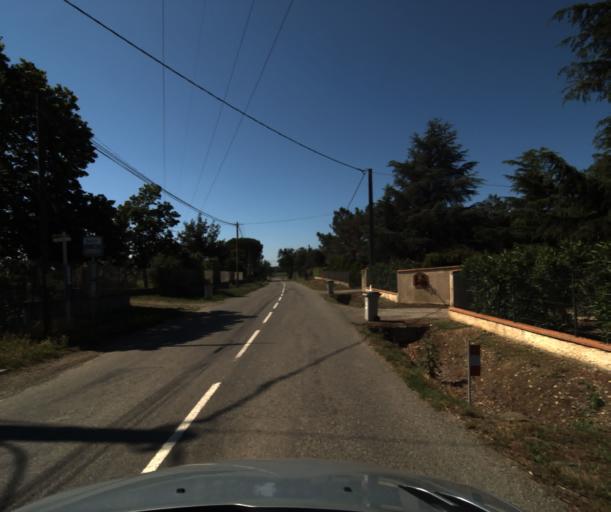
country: FR
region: Midi-Pyrenees
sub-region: Departement de la Haute-Garonne
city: Saubens
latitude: 43.4886
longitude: 1.3518
